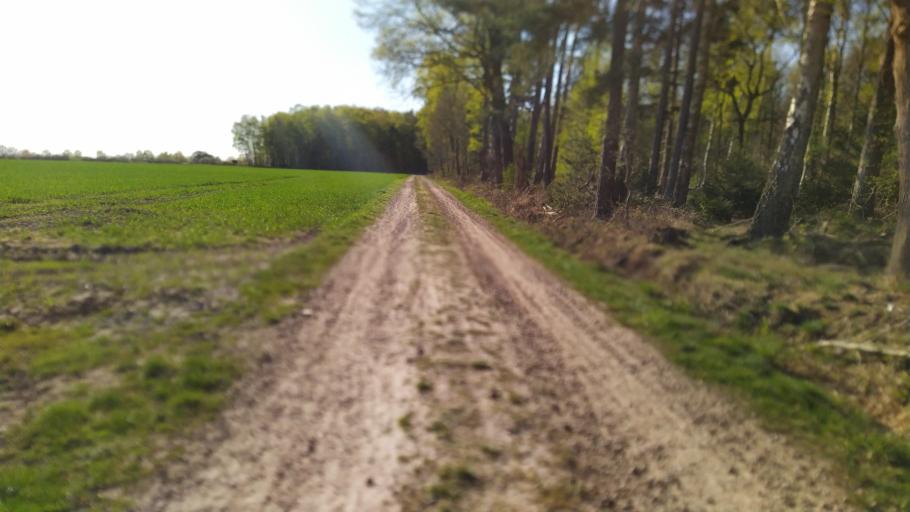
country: DE
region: Lower Saxony
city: Gross Meckelsen
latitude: 53.2897
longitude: 9.4758
